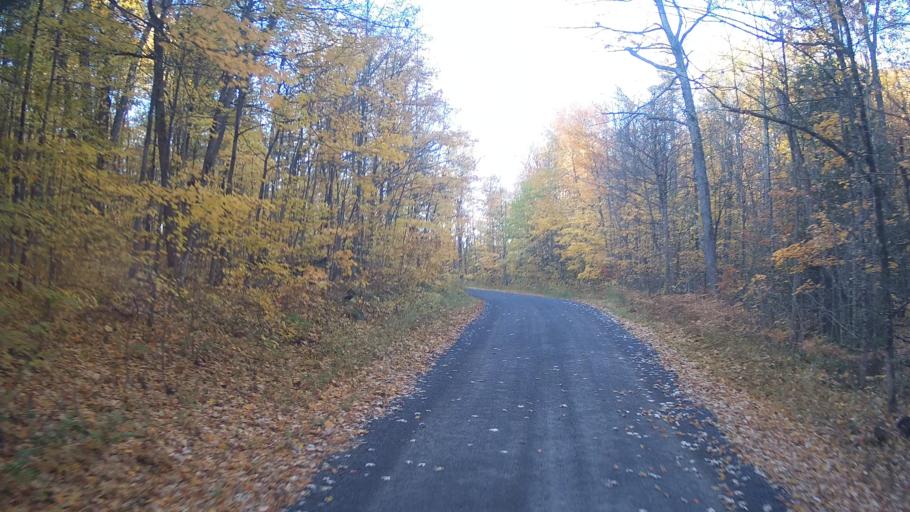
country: CA
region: Ontario
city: Arnprior
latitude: 45.3321
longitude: -76.3664
